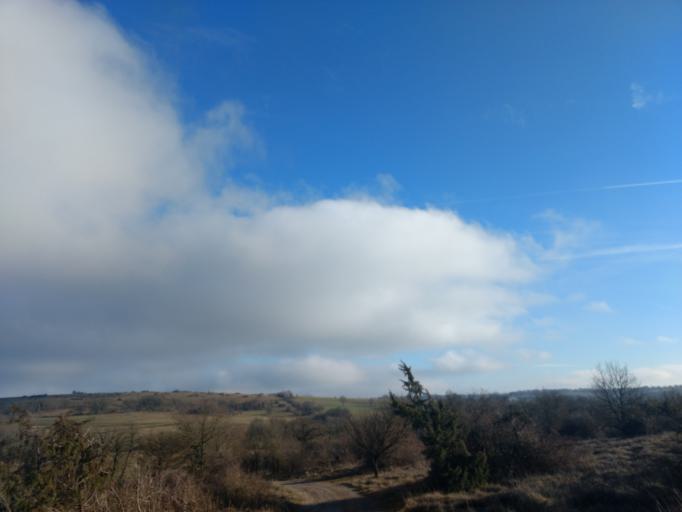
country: FR
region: Midi-Pyrenees
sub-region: Departement de l'Aveyron
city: Salles-la-Source
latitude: 44.4348
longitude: 2.5259
